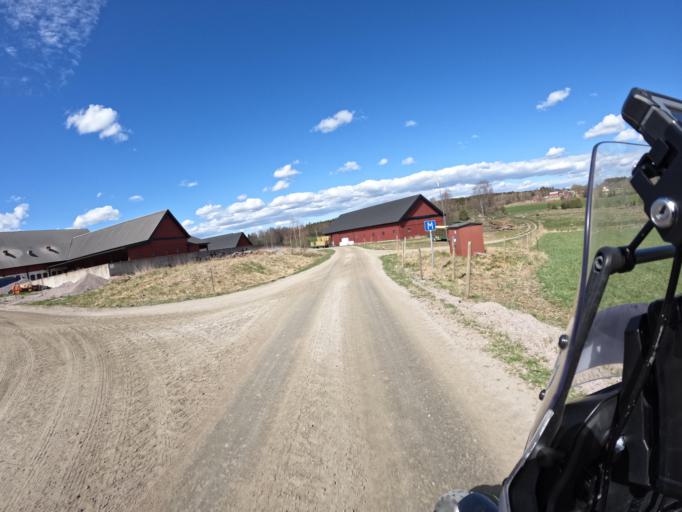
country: SE
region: Vaestra Goetaland
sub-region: Ulricehamns Kommun
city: Ulricehamn
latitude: 57.9019
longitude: 13.4476
